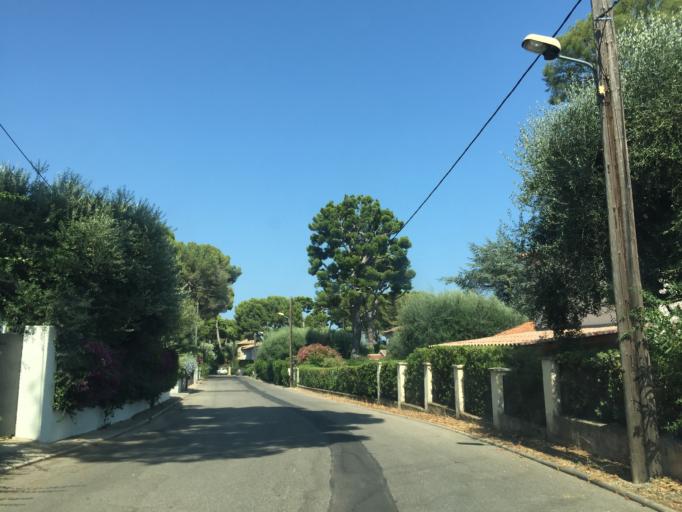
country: FR
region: Provence-Alpes-Cote d'Azur
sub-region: Departement des Alpes-Maritimes
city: Antibes
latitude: 43.5618
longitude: 7.1333
